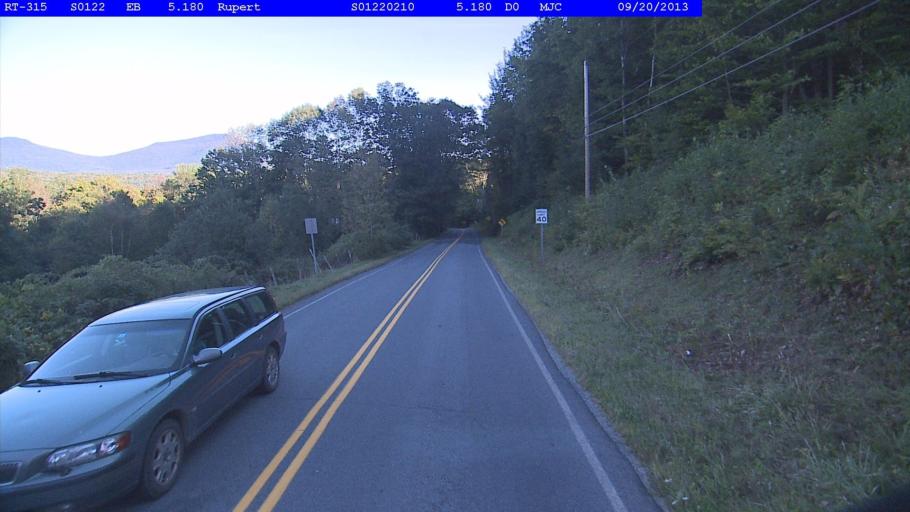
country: US
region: Vermont
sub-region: Bennington County
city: Manchester Center
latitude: 43.2767
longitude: -73.1360
